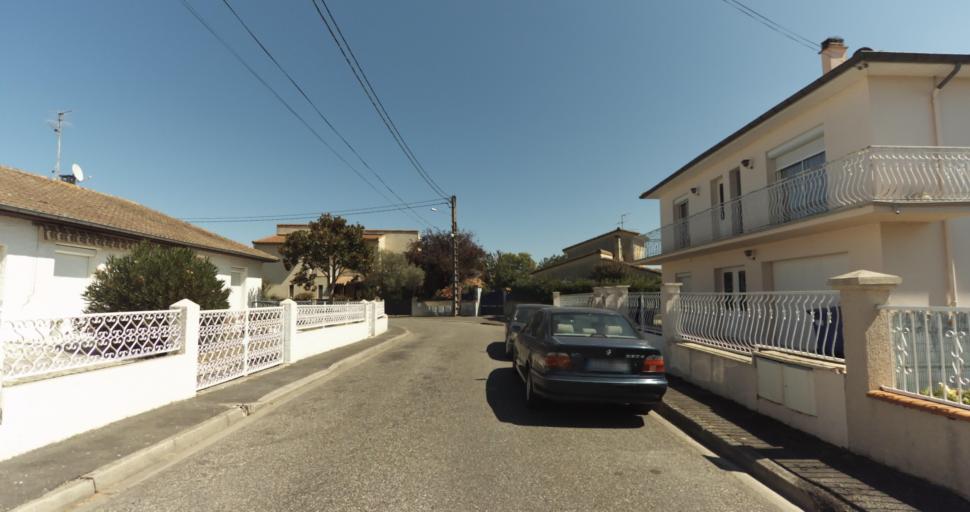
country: FR
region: Midi-Pyrenees
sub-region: Departement de la Haute-Garonne
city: L'Union
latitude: 43.6492
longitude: 1.4823
